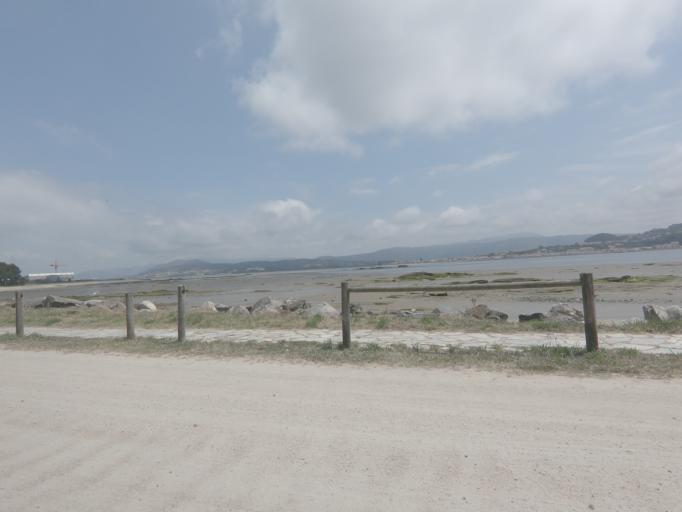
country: ES
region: Galicia
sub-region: Provincia de Pontevedra
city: A Guarda
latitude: 41.8821
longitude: -8.8592
